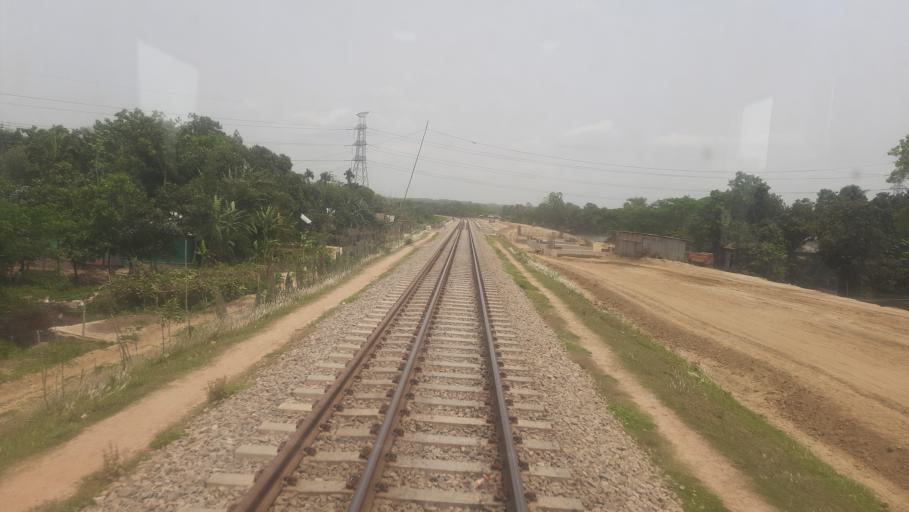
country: IN
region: Tripura
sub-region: West Tripura
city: Agartala
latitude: 23.6740
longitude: 91.1570
